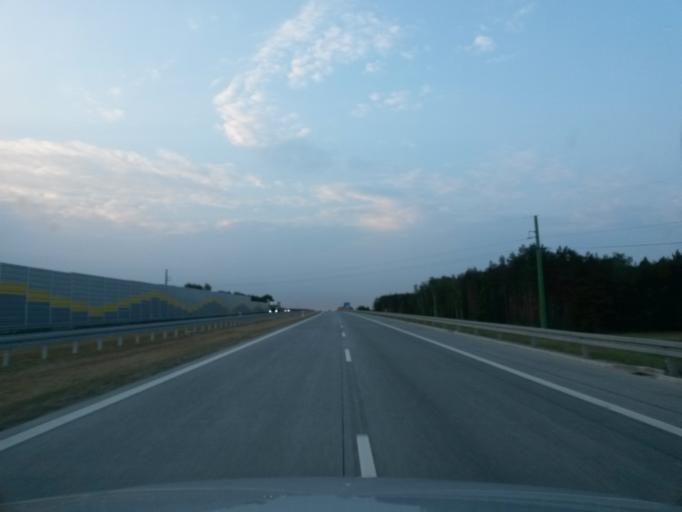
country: PL
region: Lodz Voivodeship
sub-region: Powiat sieradzki
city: Brzeznio
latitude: 51.5046
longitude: 18.6907
